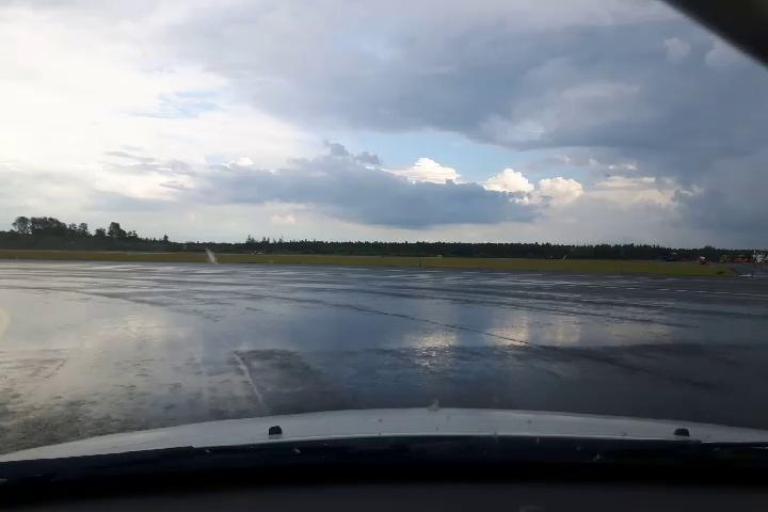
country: SE
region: Stockholm
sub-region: Sigtuna Kommun
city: Rosersberg
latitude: 59.6288
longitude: 17.9494
